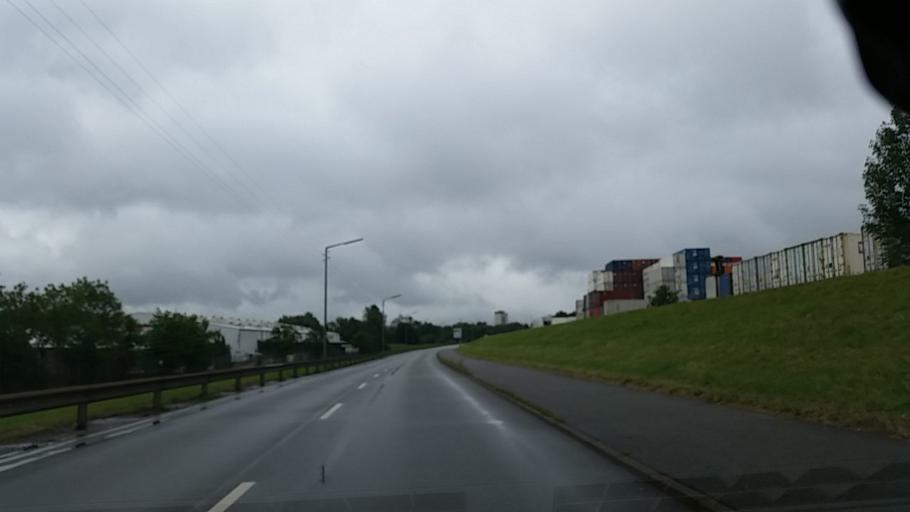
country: DE
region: Hamburg
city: Kleiner Grasbrook
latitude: 53.5148
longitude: 9.9786
